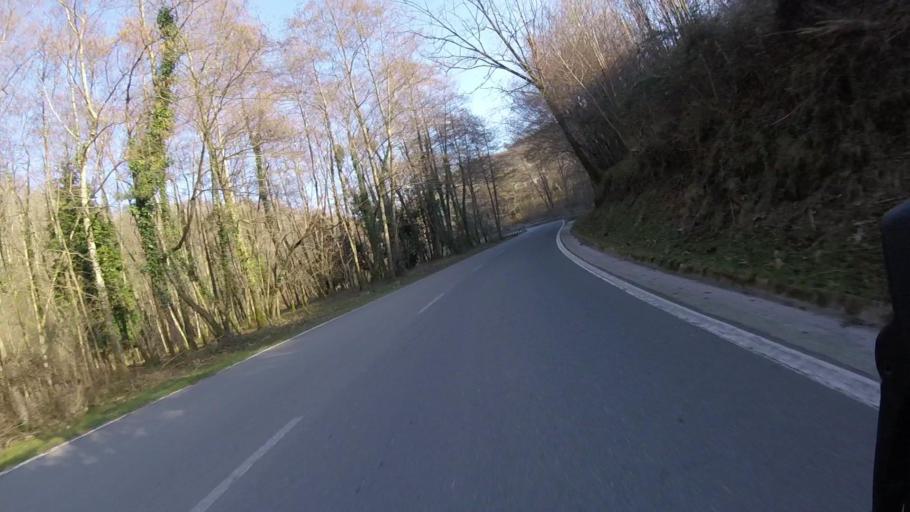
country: ES
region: Navarre
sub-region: Provincia de Navarra
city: Arano
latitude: 43.2120
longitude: -1.8807
